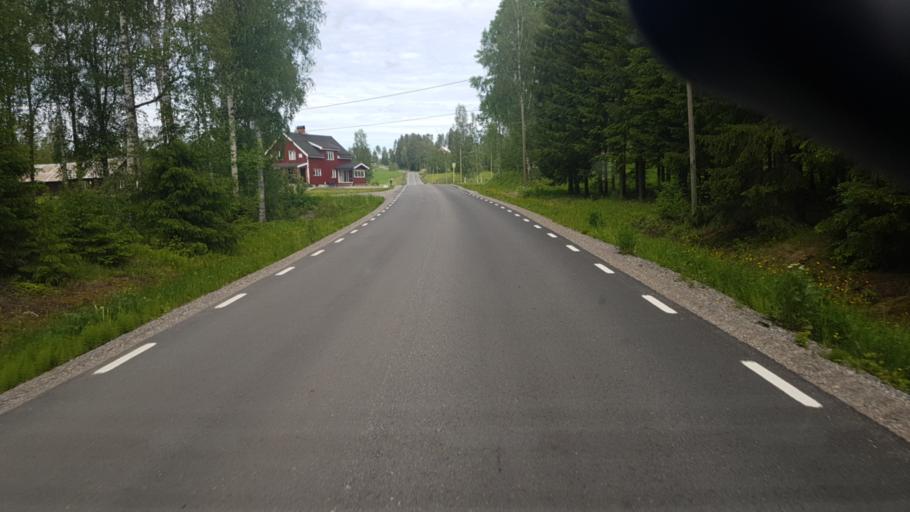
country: SE
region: Vaermland
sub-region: Eda Kommun
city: Amotfors
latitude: 59.9094
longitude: 12.5240
